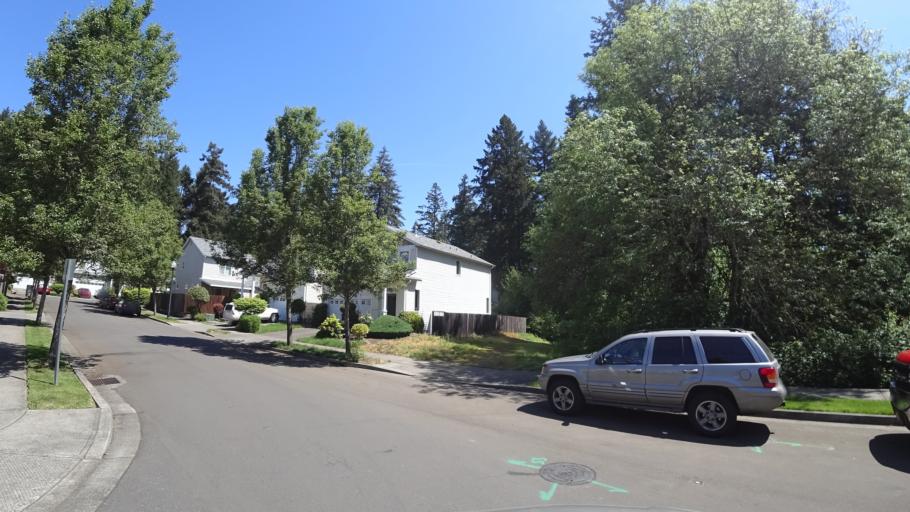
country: US
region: Oregon
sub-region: Washington County
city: Rockcreek
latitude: 45.5247
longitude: -122.9238
